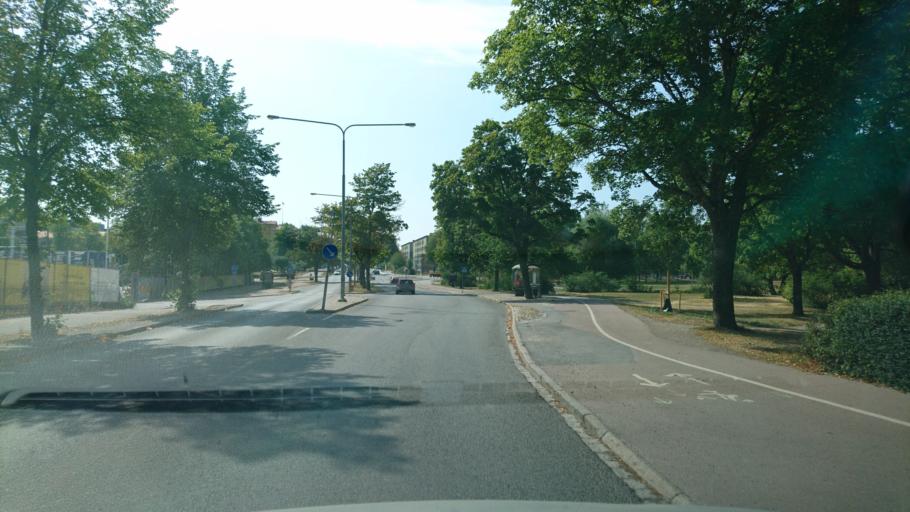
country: SE
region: Uppsala
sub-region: Uppsala Kommun
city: Uppsala
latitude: 59.8476
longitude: 17.6370
